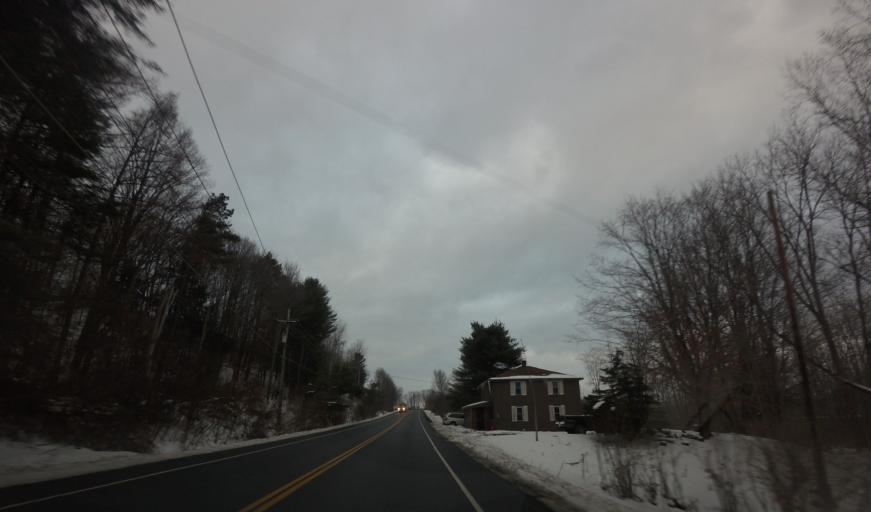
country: US
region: New York
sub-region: Tompkins County
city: Dryden
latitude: 42.5448
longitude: -76.2964
